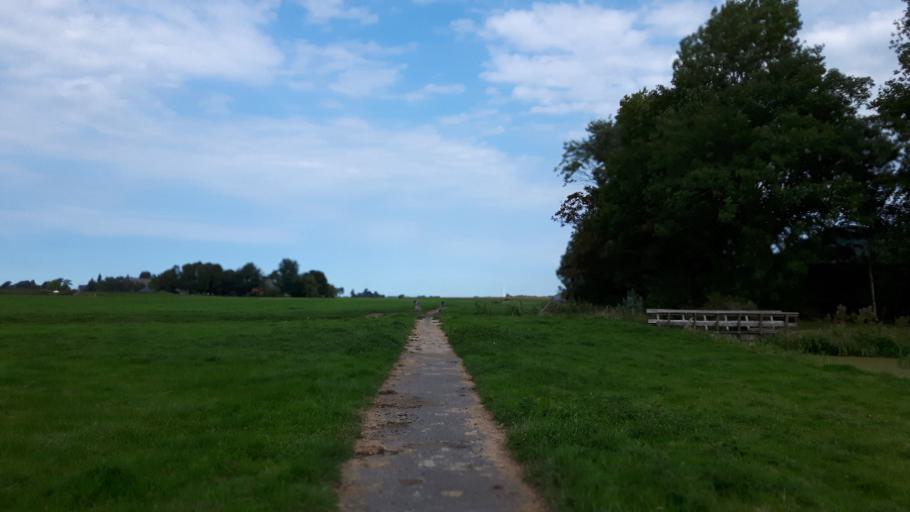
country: NL
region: Friesland
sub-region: Gemeente Leeuwarden
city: Camminghaburen
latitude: 53.2369
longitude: 5.8294
